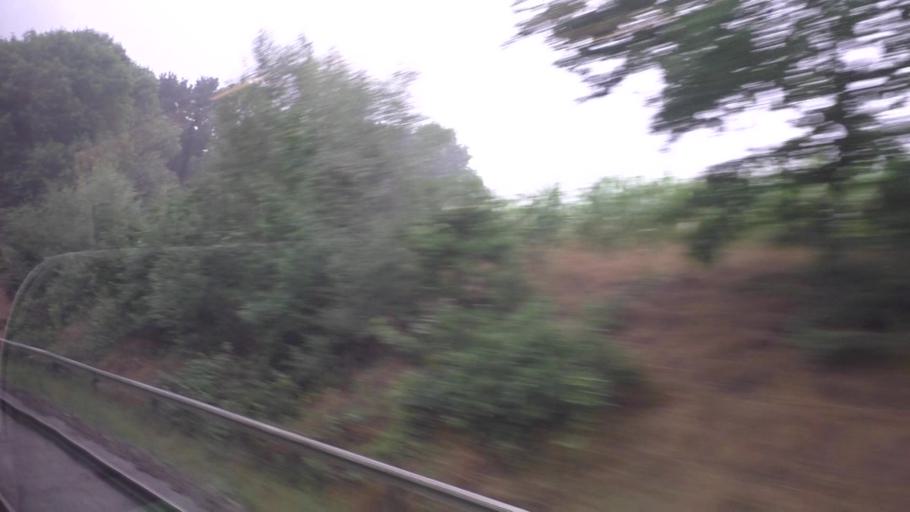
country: DE
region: Saxony
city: Arnsdorf
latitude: 51.1000
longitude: 13.9605
